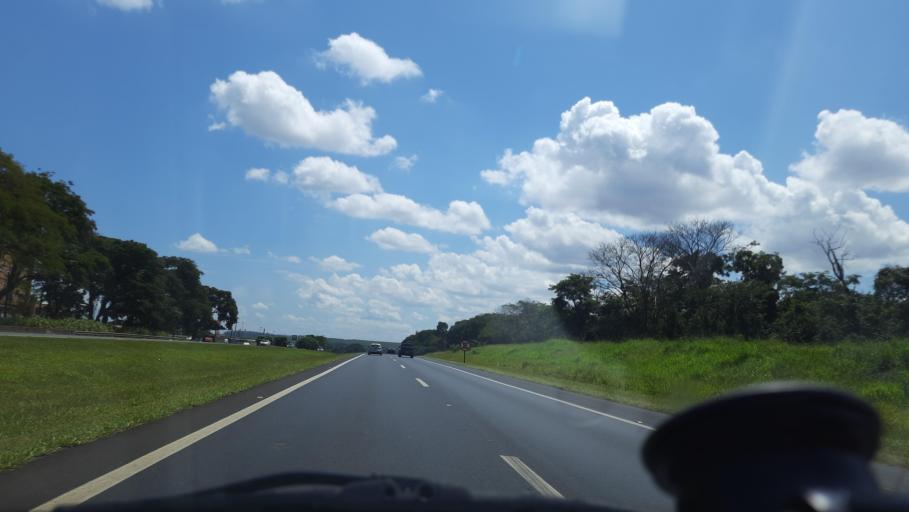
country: BR
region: Sao Paulo
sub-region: Moji-Guacu
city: Mogi-Gaucu
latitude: -22.3796
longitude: -46.9711
